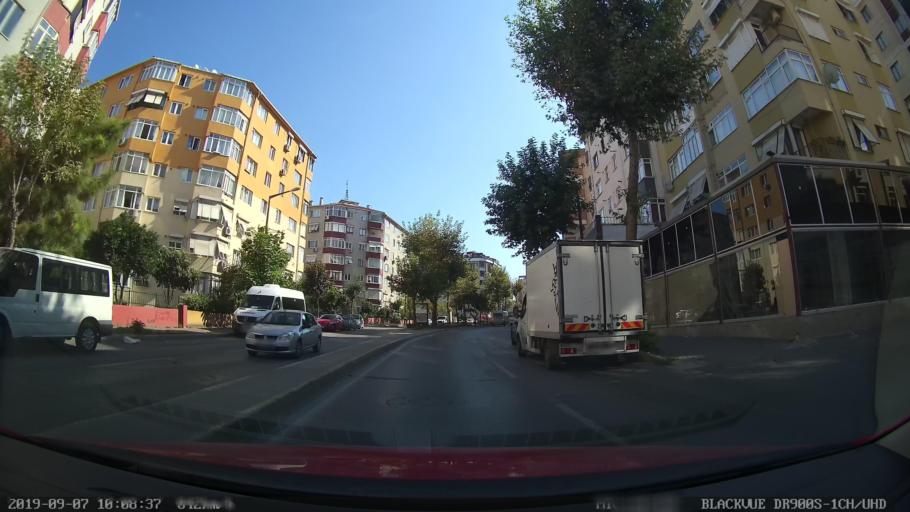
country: TR
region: Istanbul
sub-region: Atasehir
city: Atasehir
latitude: 40.9492
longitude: 29.1160
